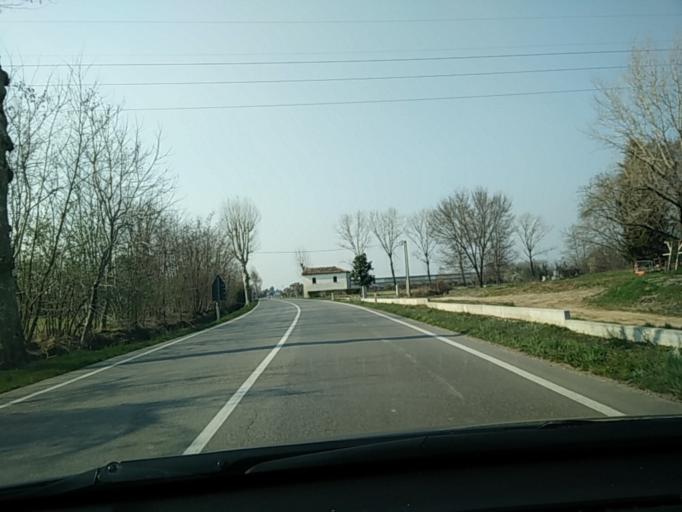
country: IT
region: Veneto
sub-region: Provincia di Treviso
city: Castagnole
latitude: 45.7066
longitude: 12.1719
